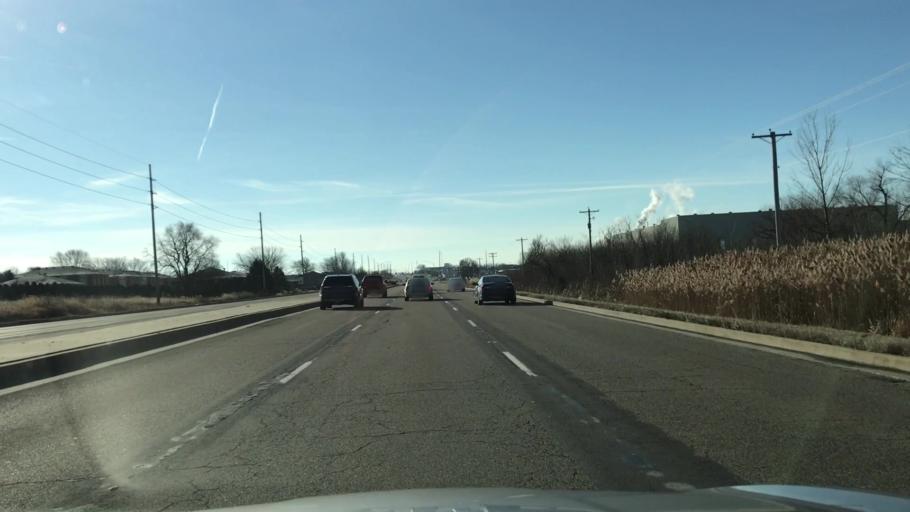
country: US
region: Illinois
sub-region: McLean County
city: Normal
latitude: 40.5235
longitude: -88.9525
